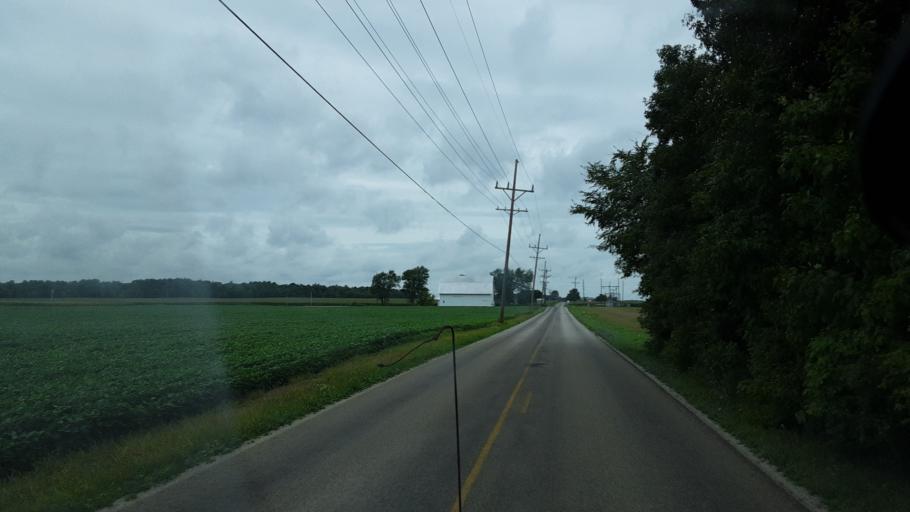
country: US
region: Indiana
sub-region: Jay County
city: Portland
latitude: 40.4645
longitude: -85.0203
